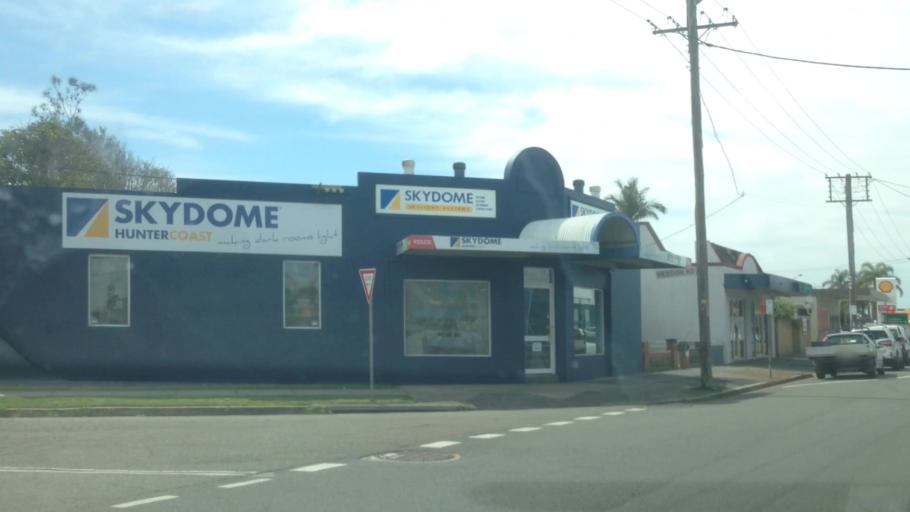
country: AU
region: New South Wales
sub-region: Newcastle
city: Broadmeadow
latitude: -32.9259
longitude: 151.7358
